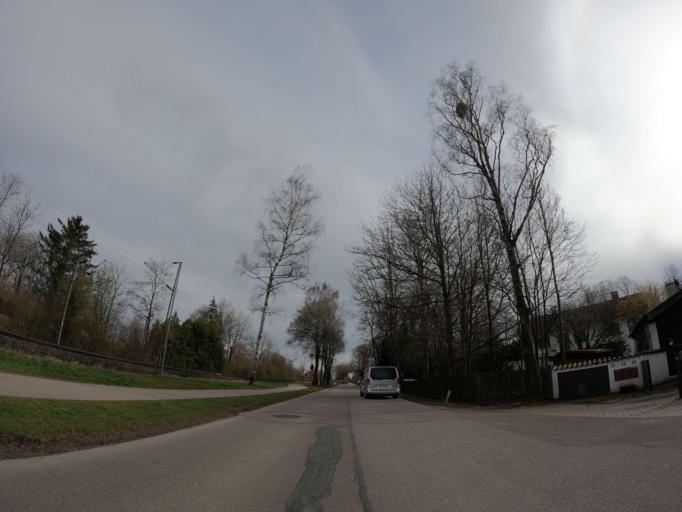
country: DE
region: Bavaria
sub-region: Upper Bavaria
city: Oberhaching
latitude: 48.0276
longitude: 11.5795
